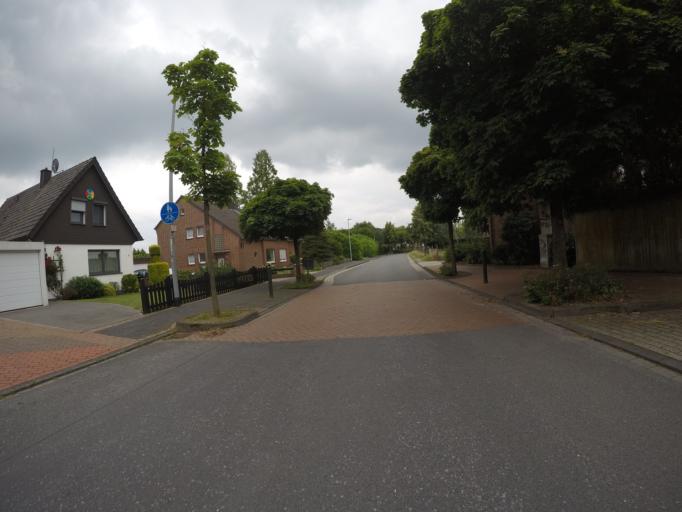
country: DE
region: North Rhine-Westphalia
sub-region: Regierungsbezirk Dusseldorf
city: Hunxe
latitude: 51.6424
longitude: 6.7699
